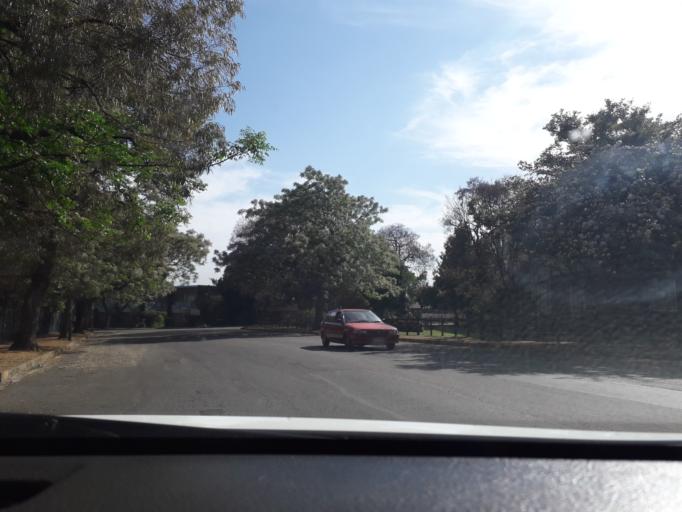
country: ZA
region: Gauteng
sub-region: City of Johannesburg Metropolitan Municipality
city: Modderfontein
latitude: -26.0932
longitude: 28.2373
